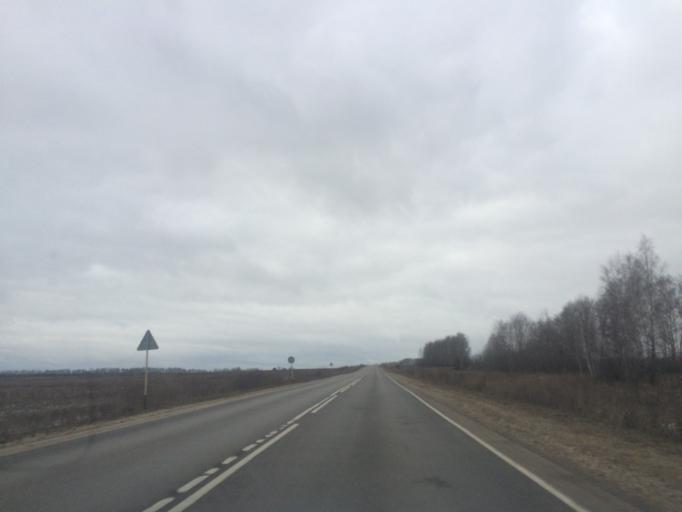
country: RU
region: Tula
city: Krapivna
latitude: 54.1130
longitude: 37.2002
